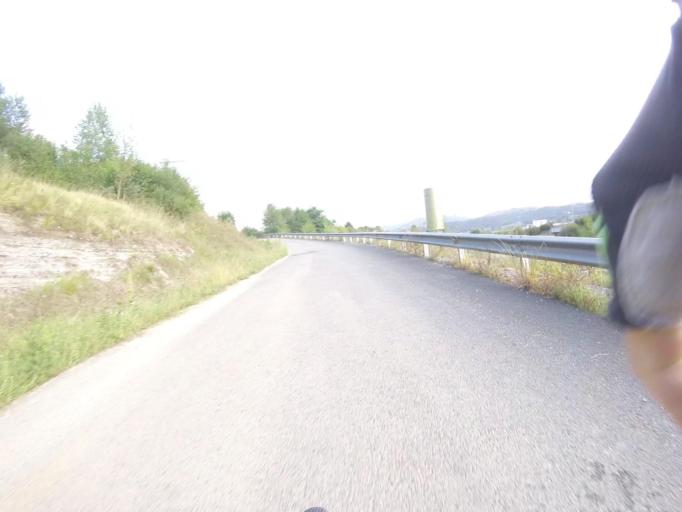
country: ES
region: Basque Country
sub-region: Provincia de Guipuzcoa
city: Irun
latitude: 43.3326
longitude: -1.8407
